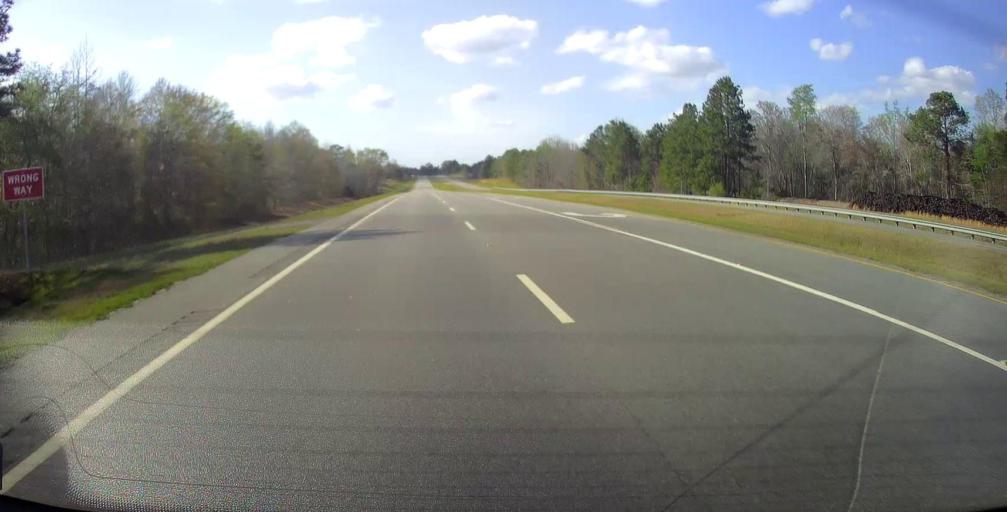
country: US
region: Georgia
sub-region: Telfair County
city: Helena
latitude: 32.0970
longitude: -82.9500
